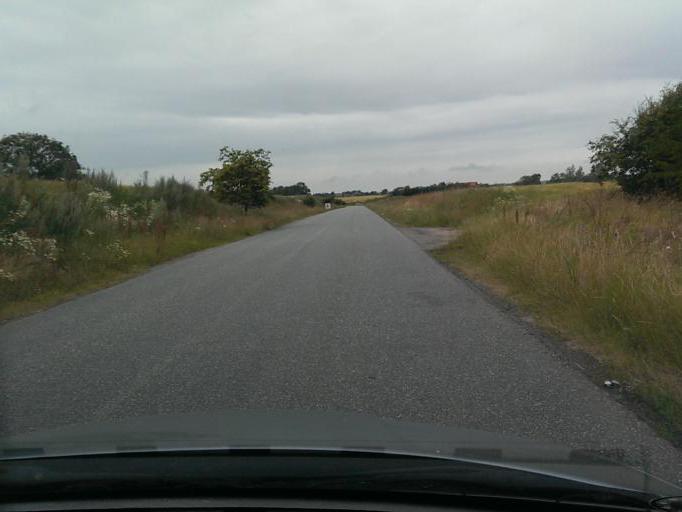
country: DK
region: North Denmark
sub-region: Hjorring Kommune
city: Vra
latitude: 57.3555
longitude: 9.9285
